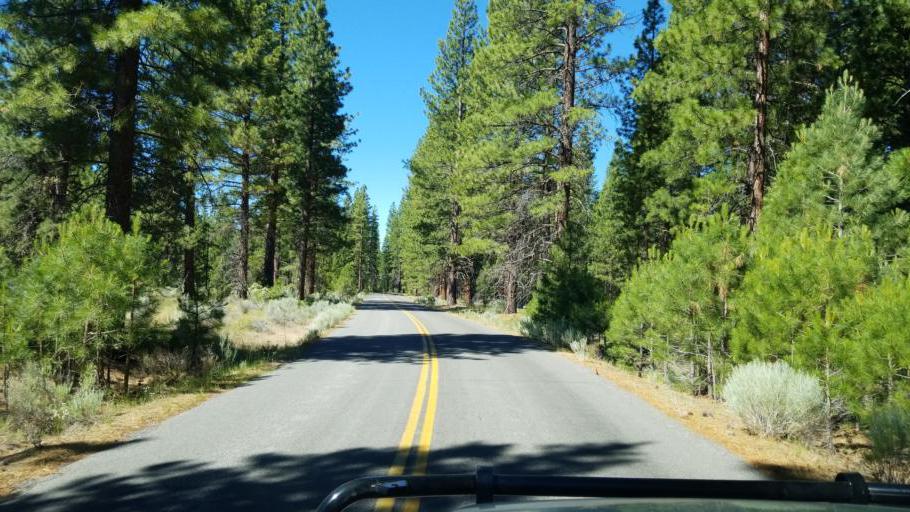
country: US
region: California
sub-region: Lassen County
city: Susanville
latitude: 40.5461
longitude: -120.7892
